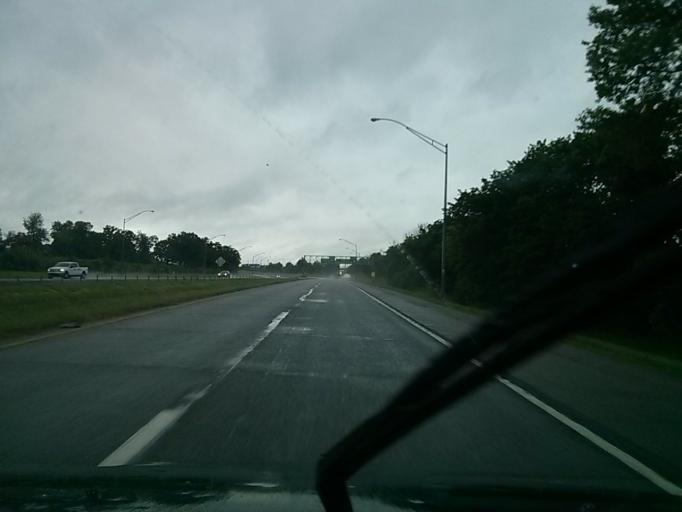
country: US
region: Oklahoma
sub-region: Tulsa County
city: Tulsa
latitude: 36.1103
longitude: -96.0154
